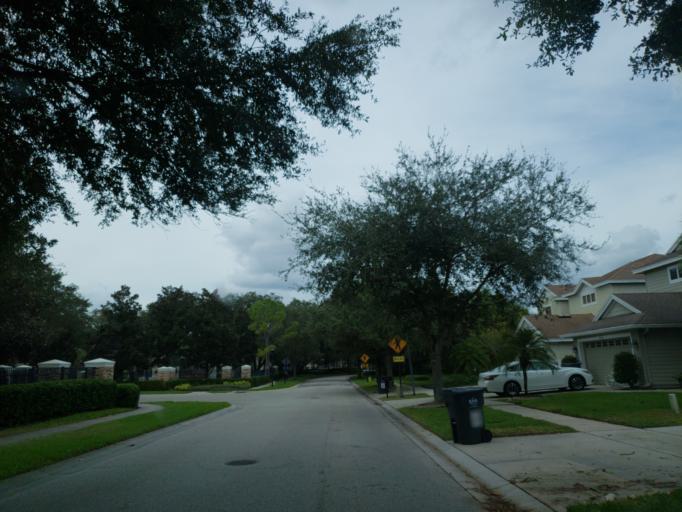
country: US
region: Florida
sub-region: Hillsborough County
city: Fish Hawk
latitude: 27.8431
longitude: -82.2284
